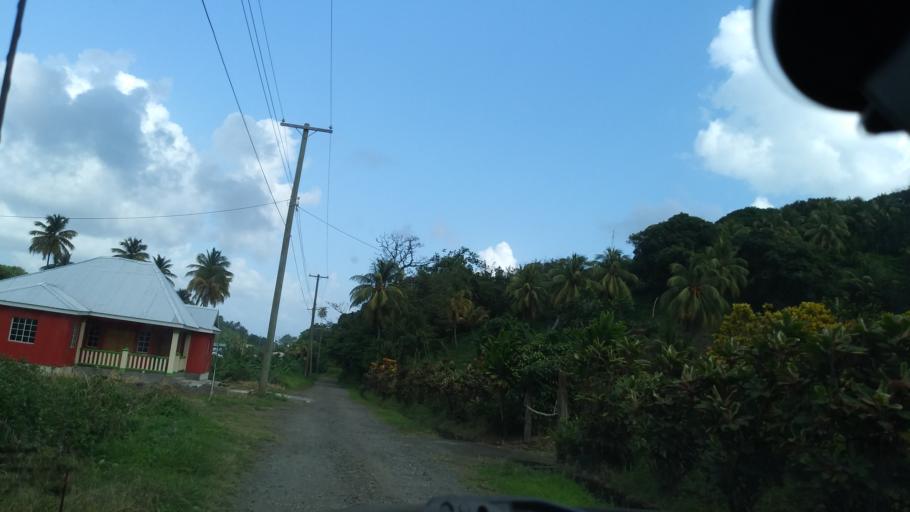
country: VC
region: Charlotte
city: Byera Village
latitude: 13.2316
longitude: -61.1315
